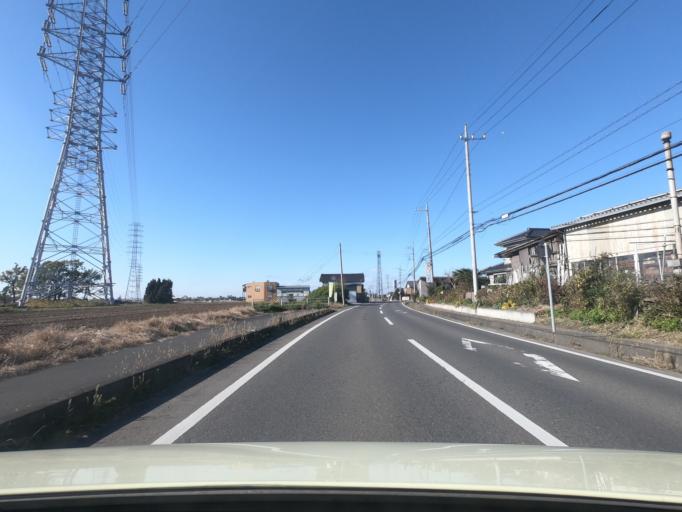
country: JP
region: Ibaraki
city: Ishige
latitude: 36.1741
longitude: 139.9799
